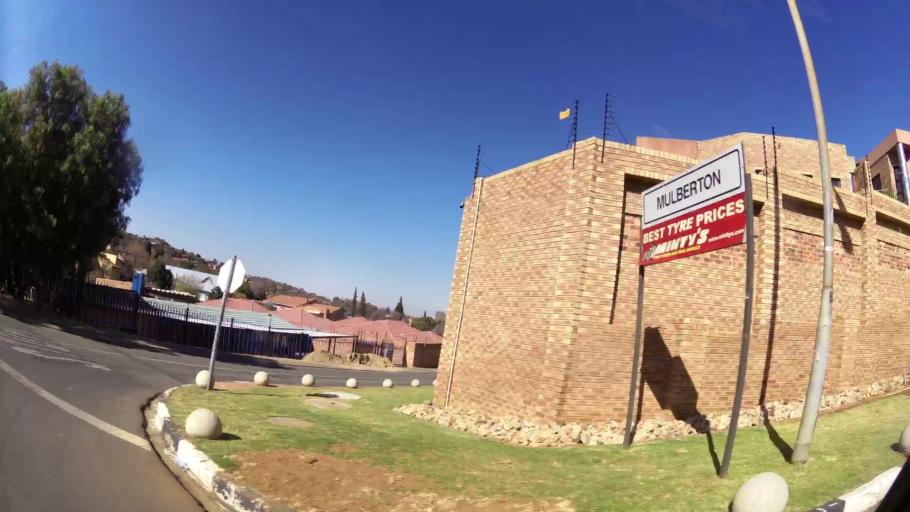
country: ZA
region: Gauteng
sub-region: City of Johannesburg Metropolitan Municipality
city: Johannesburg
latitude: -26.2874
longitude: 28.0524
